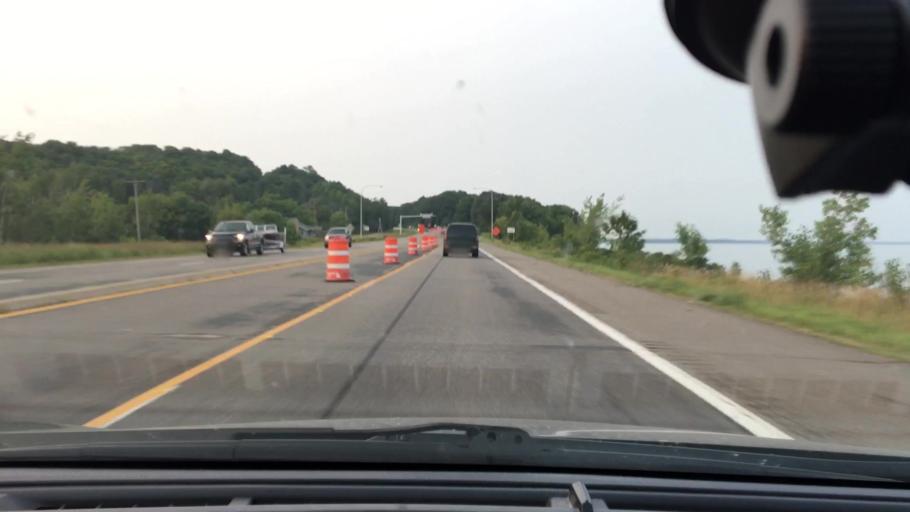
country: US
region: Minnesota
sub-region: Mille Lacs County
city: Vineland
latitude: 46.2754
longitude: -93.8215
